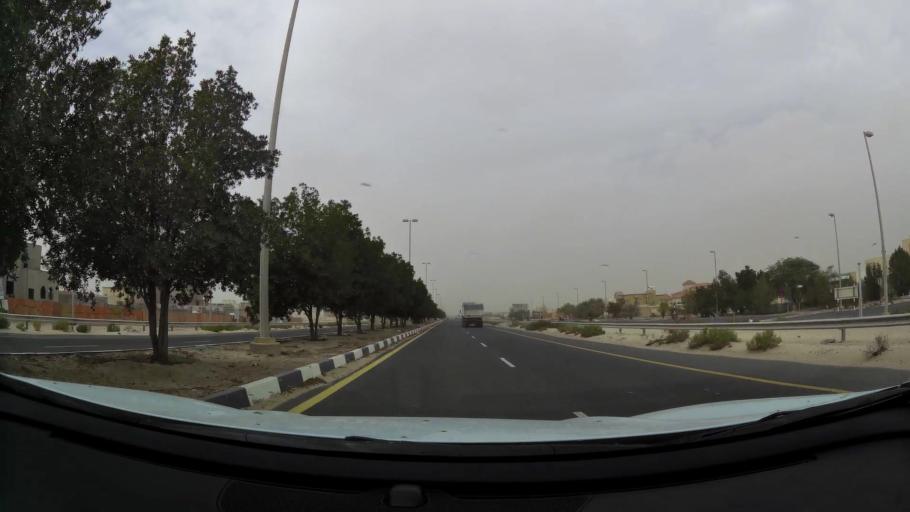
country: AE
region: Abu Dhabi
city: Abu Dhabi
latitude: 24.3653
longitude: 54.7105
